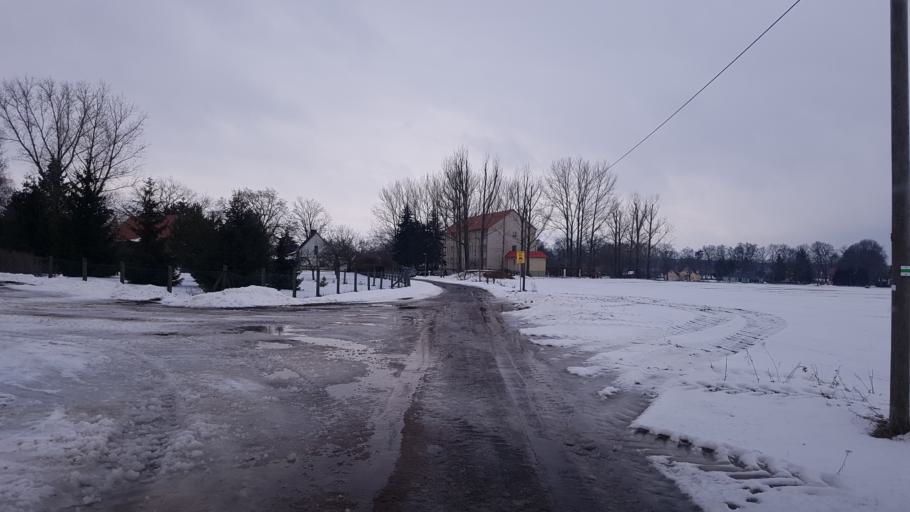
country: DE
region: Brandenburg
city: Bronkow
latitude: 51.6507
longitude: 13.9301
